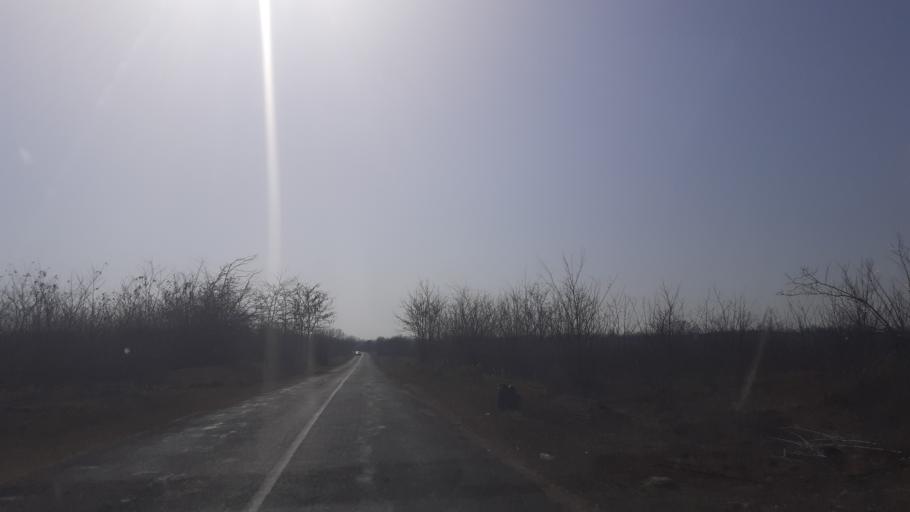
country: HU
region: Pest
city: Dabas
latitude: 47.1455
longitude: 19.3286
